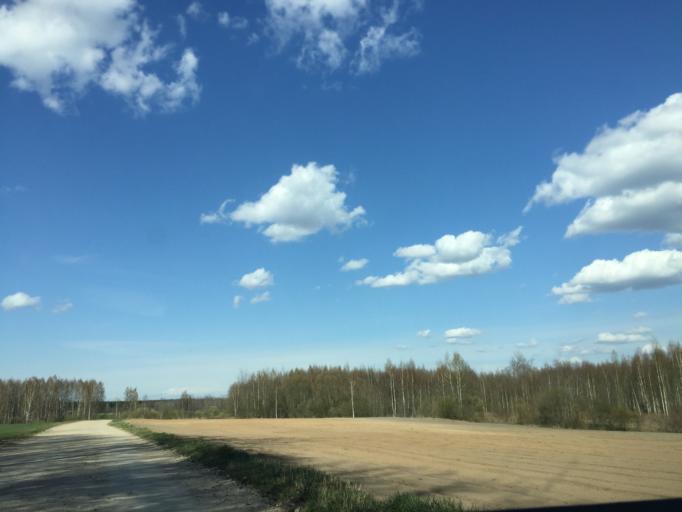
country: LV
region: Kegums
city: Kegums
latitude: 56.8260
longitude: 24.7933
